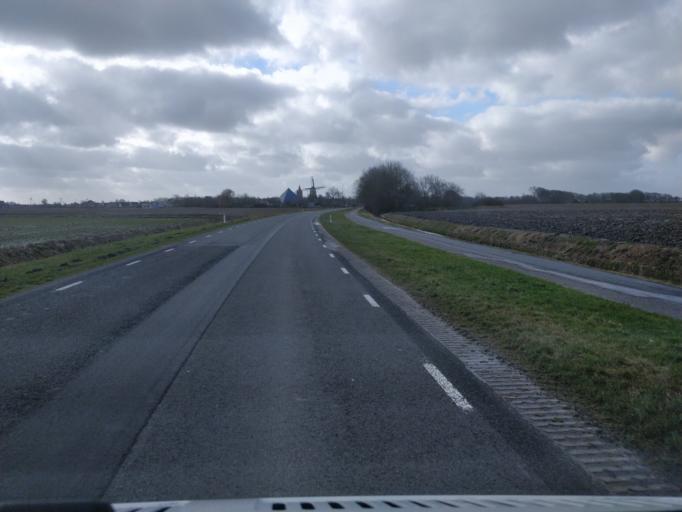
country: NL
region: Friesland
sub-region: Gemeente Franekeradeel
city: Sexbierum
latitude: 53.2255
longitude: 5.4941
